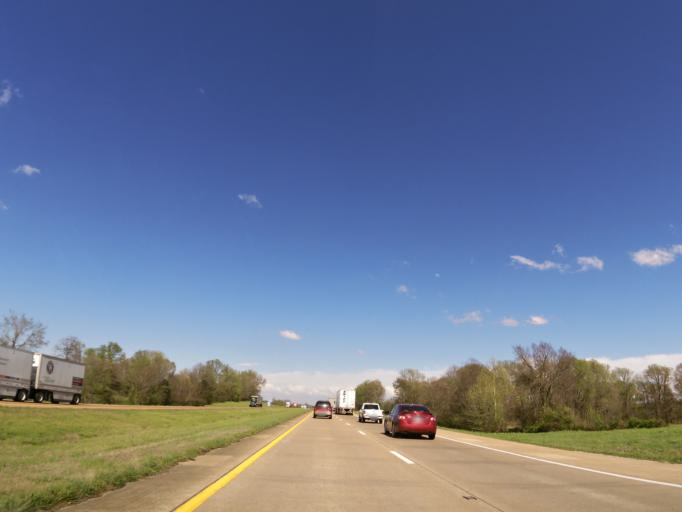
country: US
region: Tennessee
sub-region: Gibson County
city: Medina
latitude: 35.7143
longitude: -88.6460
